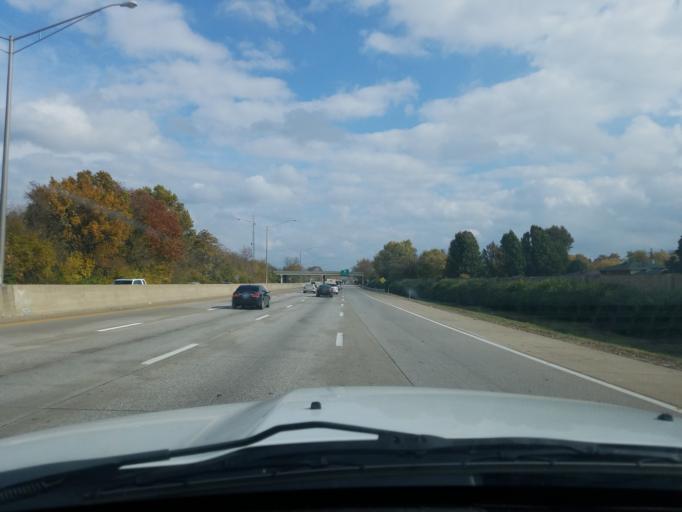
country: US
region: Kentucky
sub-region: Jefferson County
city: Shively
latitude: 38.1858
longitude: -85.8050
